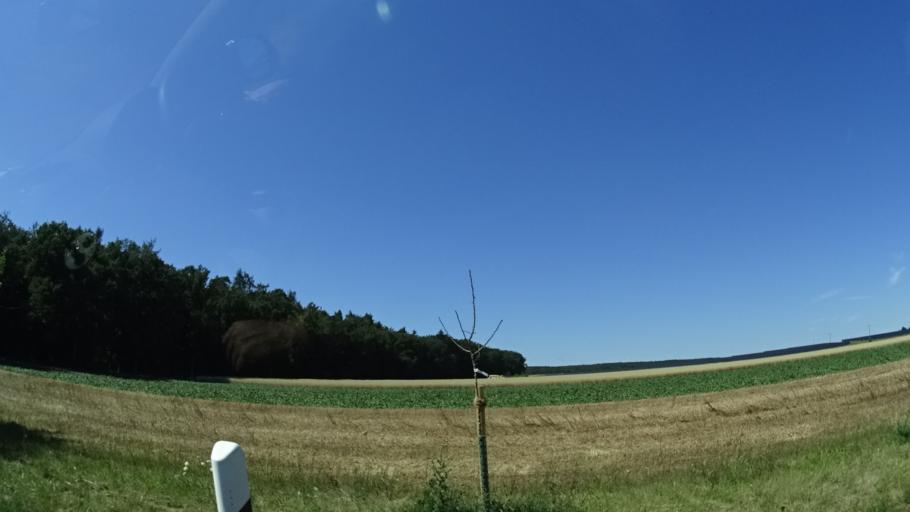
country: DE
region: Bavaria
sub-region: Regierungsbezirk Unterfranken
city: Gadheim
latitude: 49.8352
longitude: 9.9034
